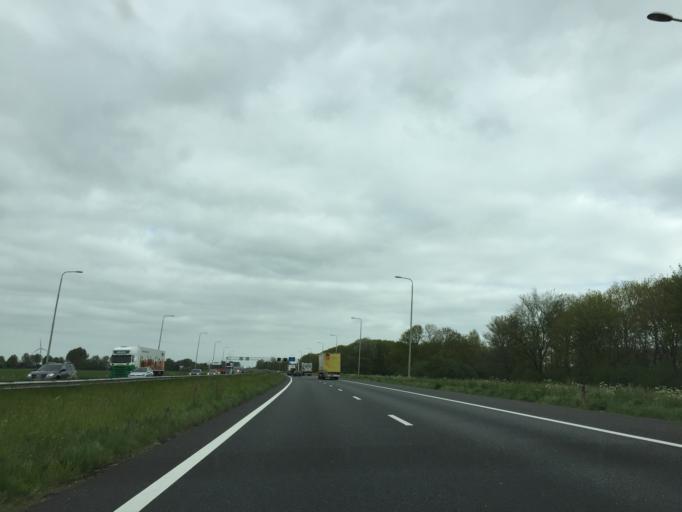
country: NL
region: North Holland
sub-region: Gemeente Hoorn
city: Hoorn
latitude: 52.6135
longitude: 5.0022
